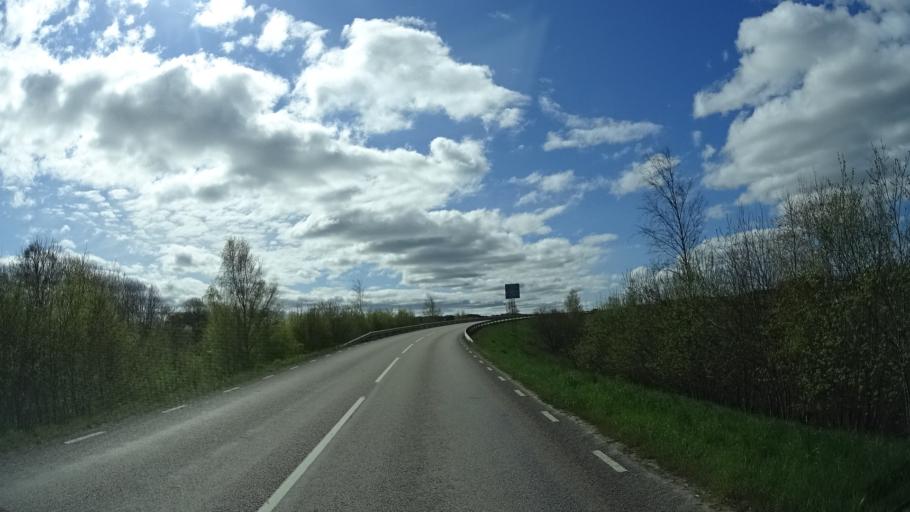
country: SE
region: Halland
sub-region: Halmstads Kommun
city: Getinge
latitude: 56.8537
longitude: 12.6812
